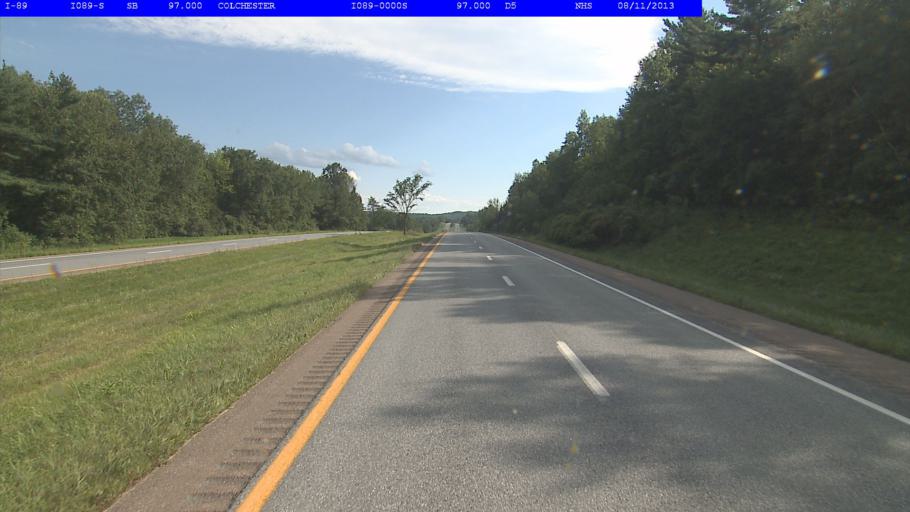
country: US
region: Vermont
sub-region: Chittenden County
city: Colchester
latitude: 44.5782
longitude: -73.1768
